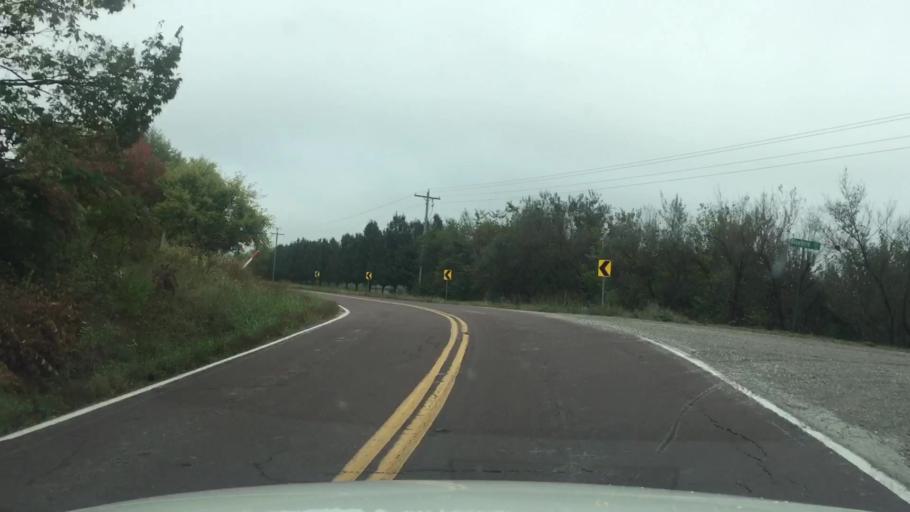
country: US
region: Missouri
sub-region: Boone County
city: Ashland
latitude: 38.8421
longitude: -92.3374
